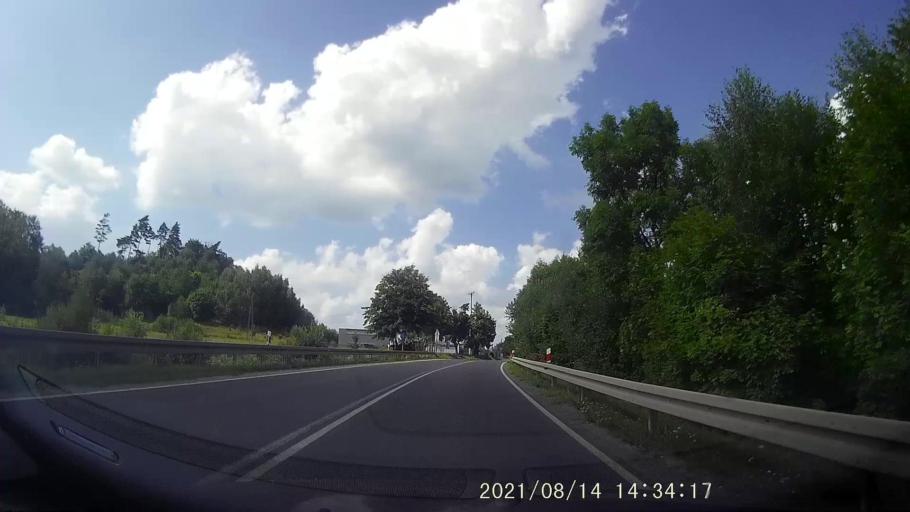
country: PL
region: Lower Silesian Voivodeship
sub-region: Powiat klodzki
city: Nowa Ruda
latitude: 50.5648
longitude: 16.5349
